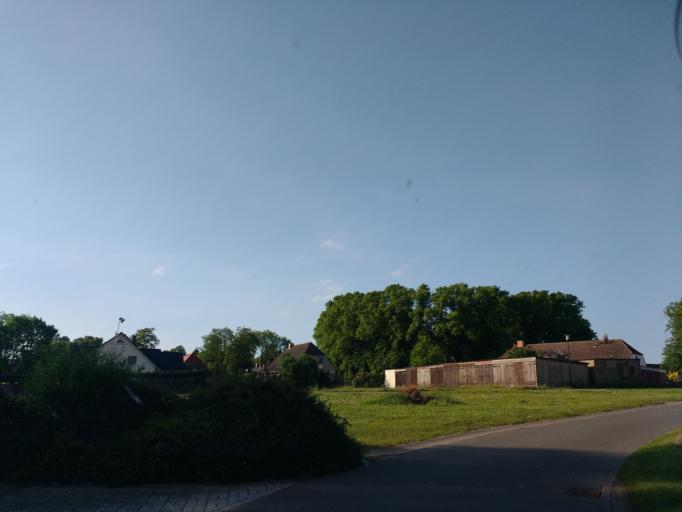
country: DE
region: Mecklenburg-Vorpommern
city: Mecklenburg
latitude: 53.8403
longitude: 11.4687
